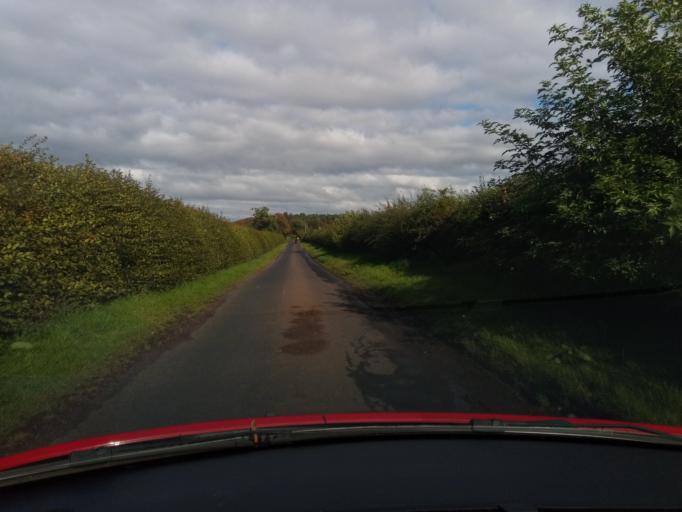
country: GB
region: Scotland
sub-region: The Scottish Borders
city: Kelso
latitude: 55.5751
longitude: -2.4038
